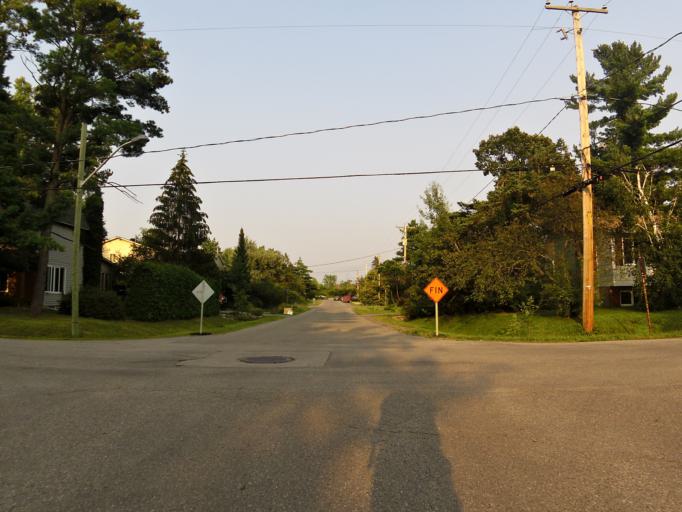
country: CA
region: Ontario
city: Bells Corners
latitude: 45.3853
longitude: -75.8357
